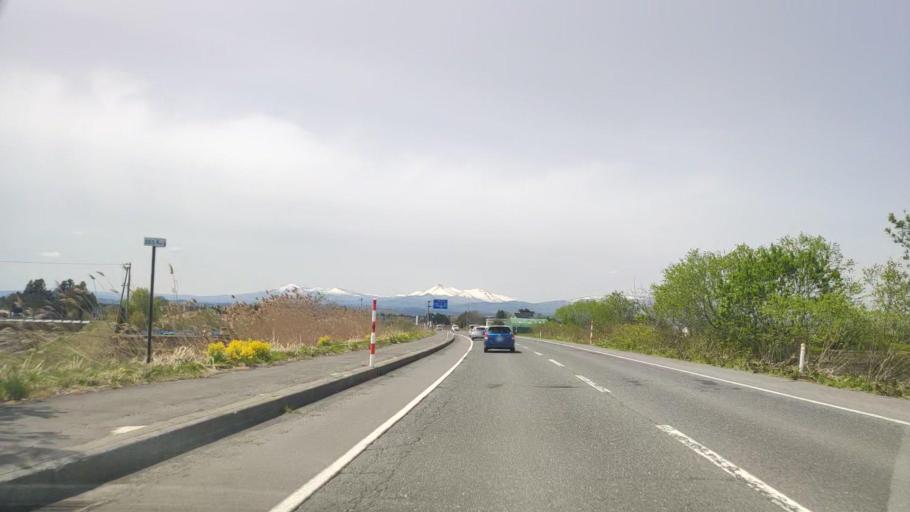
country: JP
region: Aomori
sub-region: Misawa Shi
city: Inuotose
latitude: 40.6390
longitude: 141.2358
